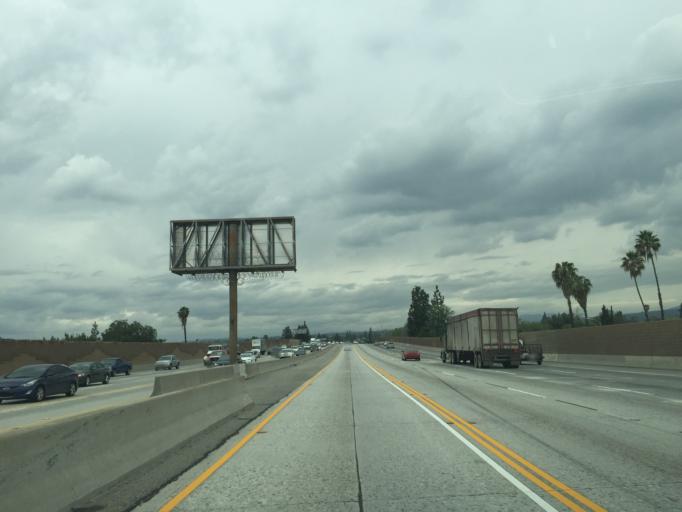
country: US
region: California
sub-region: Los Angeles County
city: Monrovia
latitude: 34.1355
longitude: -117.9970
